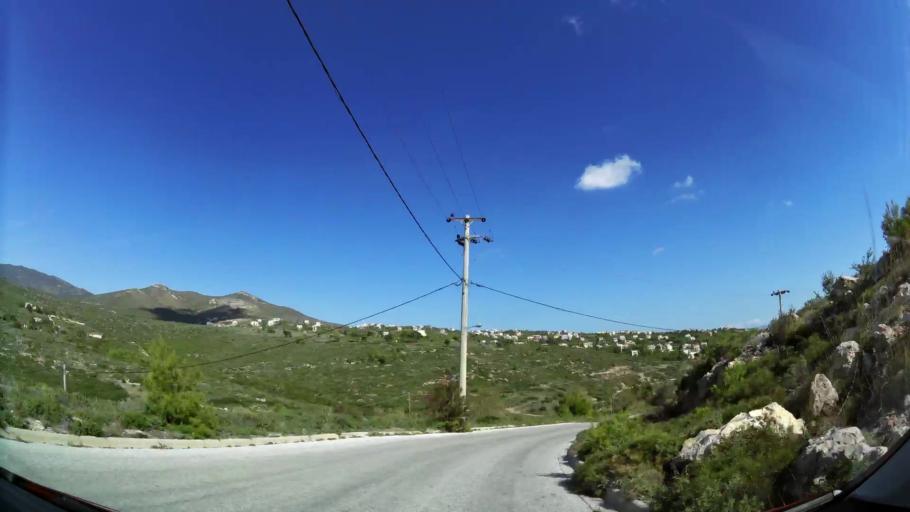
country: GR
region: Attica
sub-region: Nomarchia Anatolikis Attikis
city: Dhrafi
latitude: 38.0212
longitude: 23.9196
